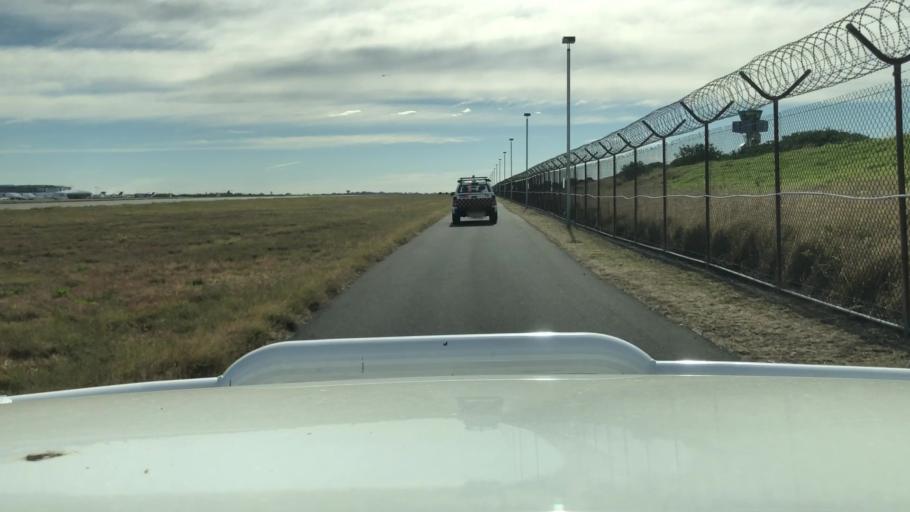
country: AU
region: New South Wales
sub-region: Botany Bay
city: Botany
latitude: -33.9496
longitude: 151.1805
